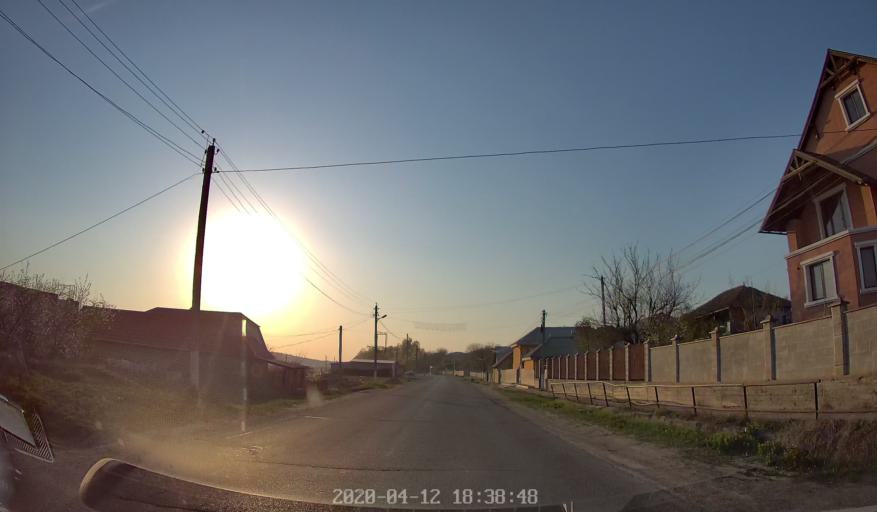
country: MD
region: Chisinau
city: Vadul lui Voda
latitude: 47.1258
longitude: 28.9960
